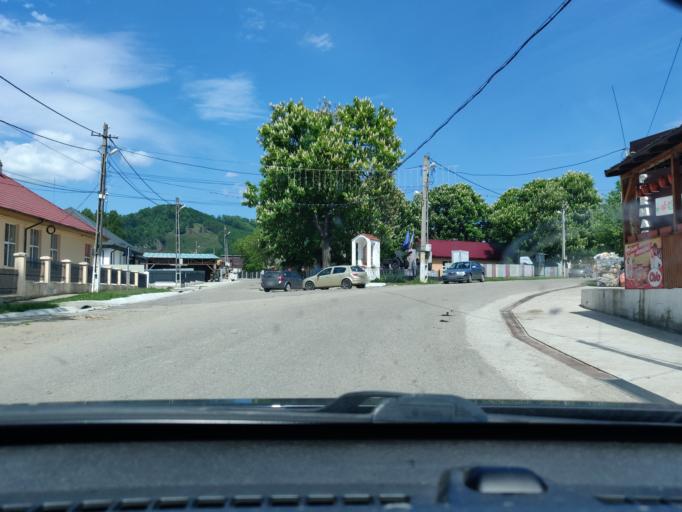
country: RO
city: Vizantea-Manastireasca
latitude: 45.9861
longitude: 26.7763
